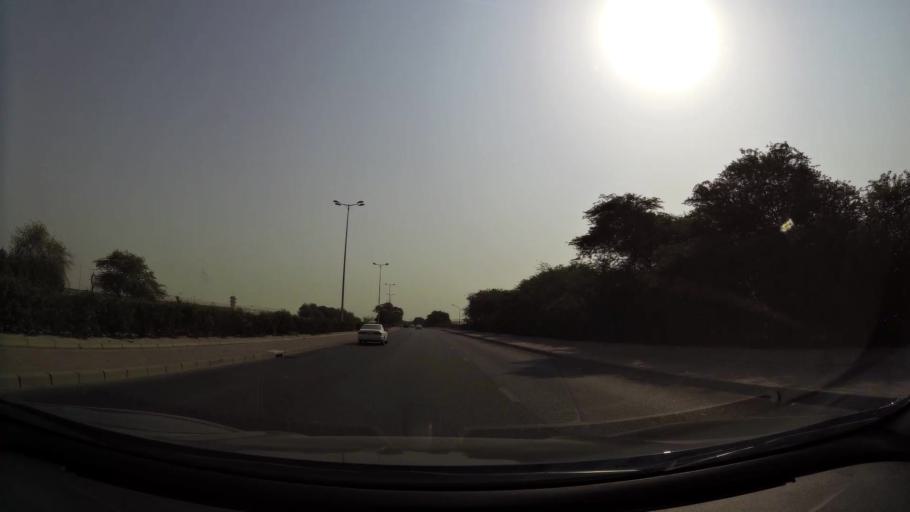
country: KW
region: Al Asimah
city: Ar Rabiyah
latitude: 29.2752
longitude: 47.8507
